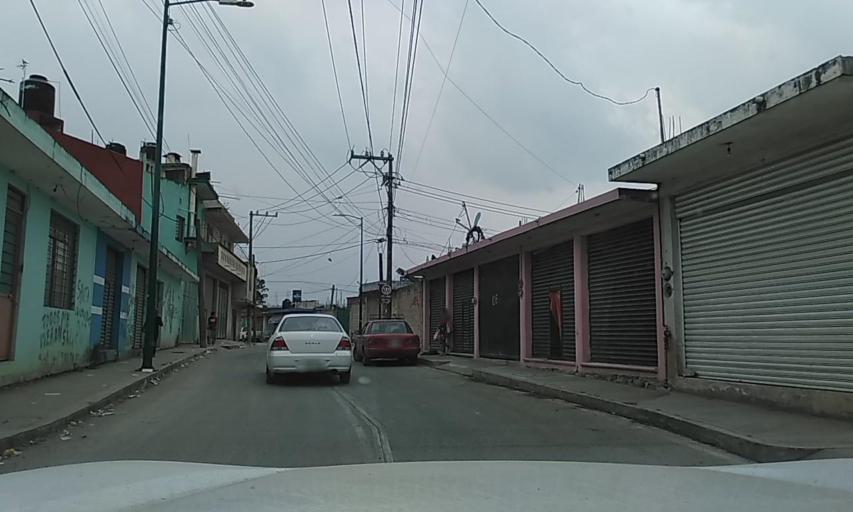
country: MX
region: Veracruz
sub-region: Jilotepec
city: El Pueblito (Garbanzal)
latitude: 19.5701
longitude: -96.8980
